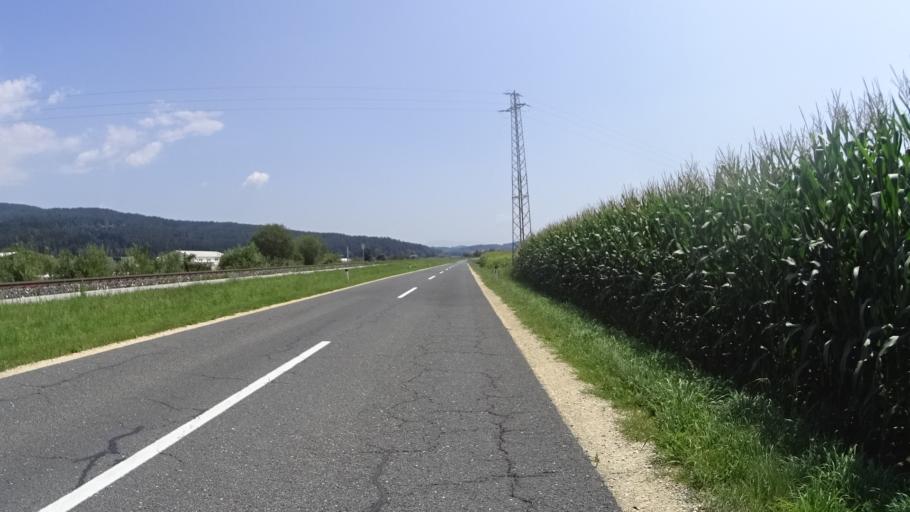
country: AT
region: Carinthia
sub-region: Politischer Bezirk Volkermarkt
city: Bleiburg/Pliberk
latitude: 46.5720
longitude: 14.7978
